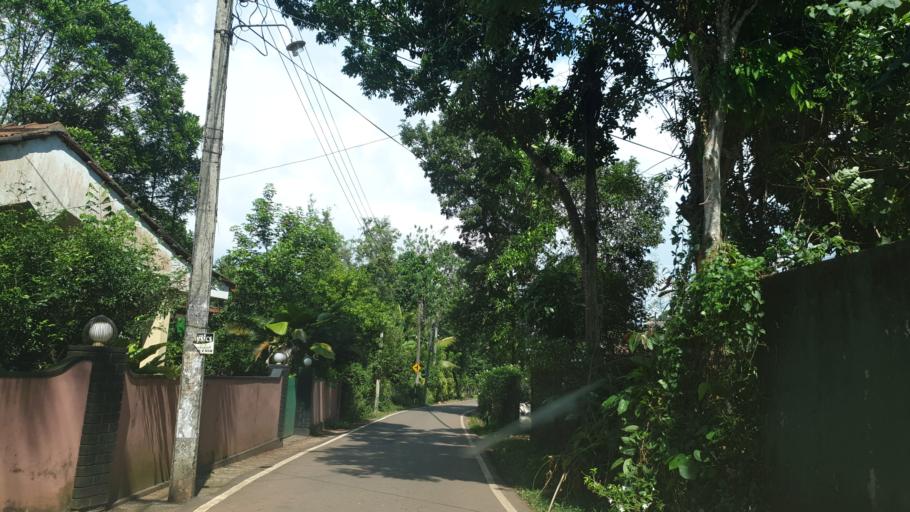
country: LK
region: Western
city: Panadura
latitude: 6.7142
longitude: 79.9624
